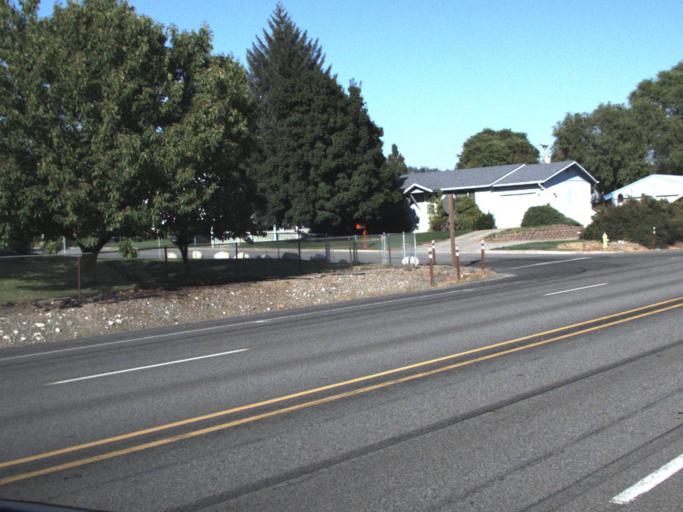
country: US
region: Washington
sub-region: Spokane County
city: Trentwood
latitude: 47.6963
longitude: -117.1846
